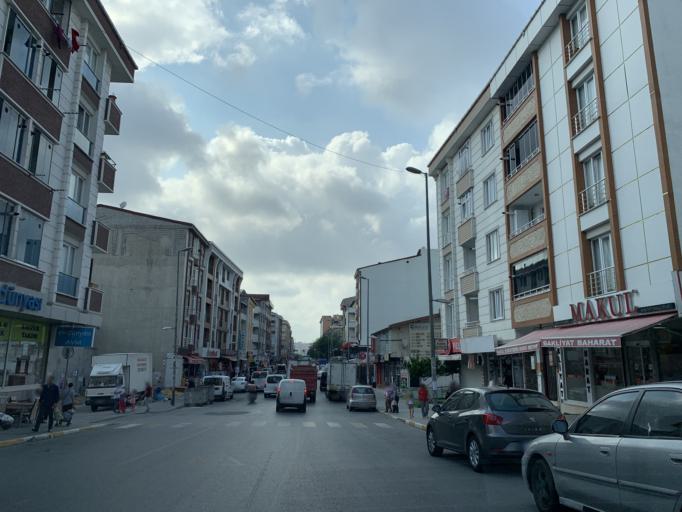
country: TR
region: Istanbul
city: Esenyurt
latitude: 41.0224
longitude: 28.6729
